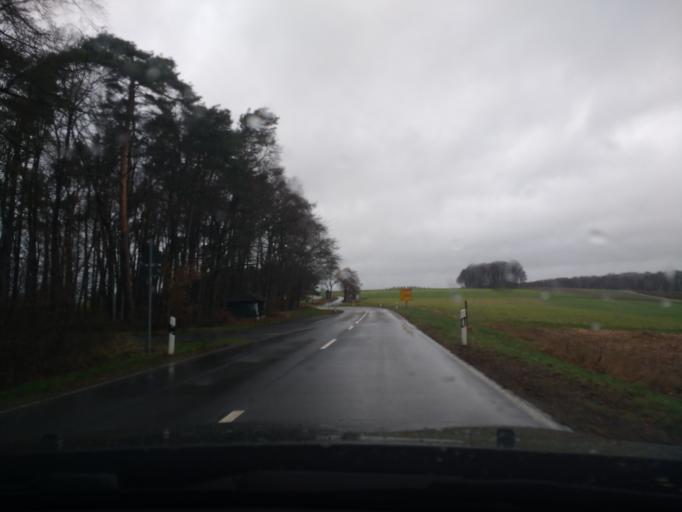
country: DE
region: Rheinland-Pfalz
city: Irmenach
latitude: 49.9387
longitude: 7.1531
